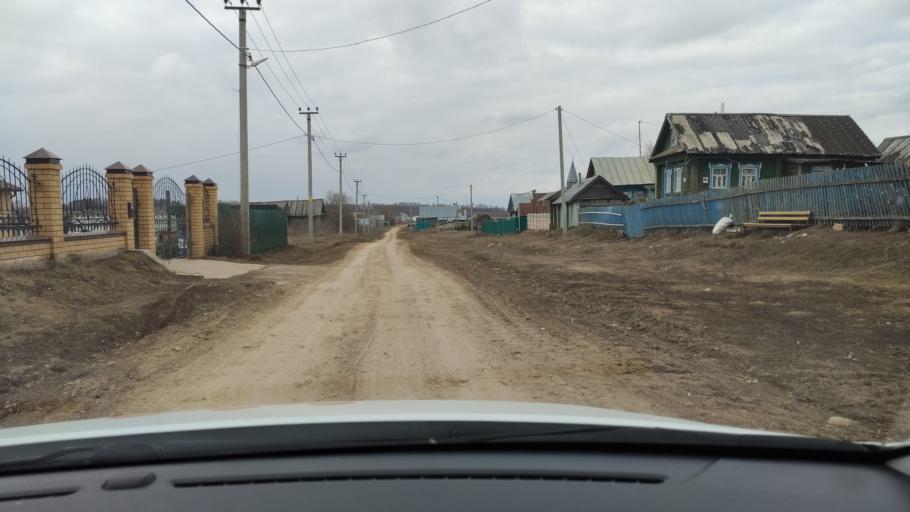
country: RU
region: Tatarstan
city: Vysokaya Gora
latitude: 56.2117
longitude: 49.3133
